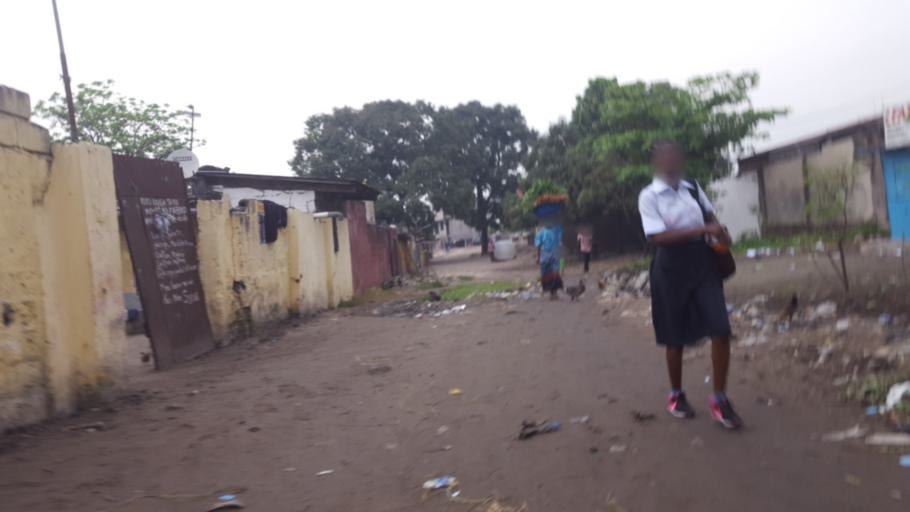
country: CD
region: Kinshasa
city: Masina
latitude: -4.3846
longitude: 15.3559
